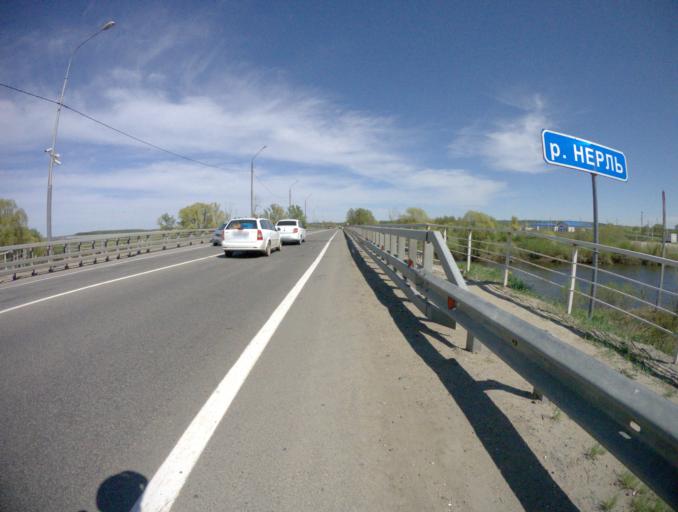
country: RU
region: Vladimir
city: Bogolyubovo
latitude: 56.2005
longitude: 40.5492
